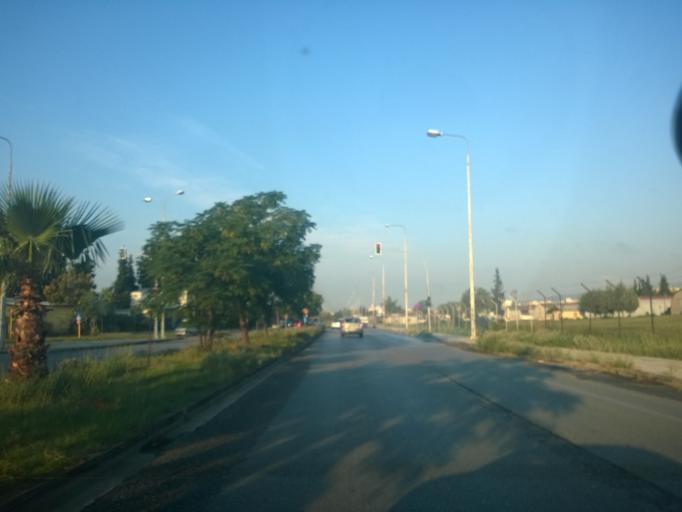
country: GR
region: Central Macedonia
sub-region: Nomos Thessalonikis
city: Ampelokipoi
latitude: 40.6612
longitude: 22.9205
